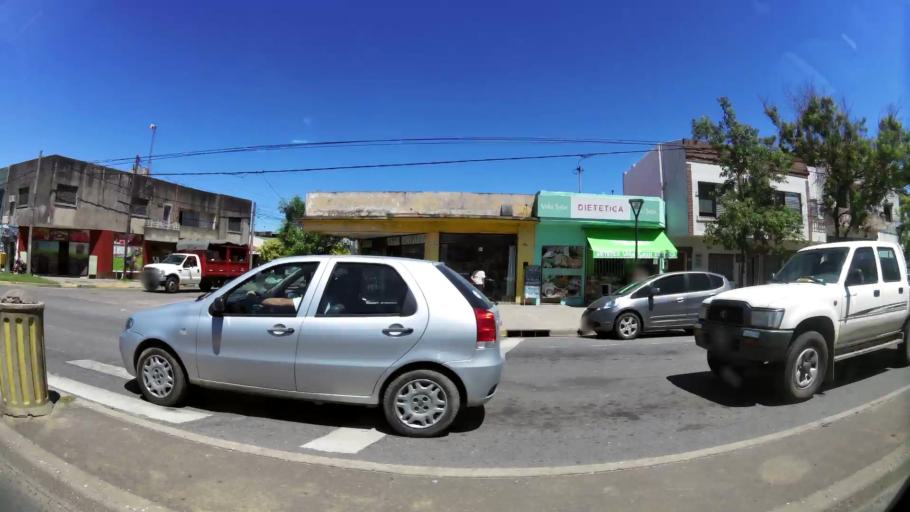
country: AR
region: Santa Fe
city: Santa Fe de la Vera Cruz
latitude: -31.6184
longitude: -60.7054
